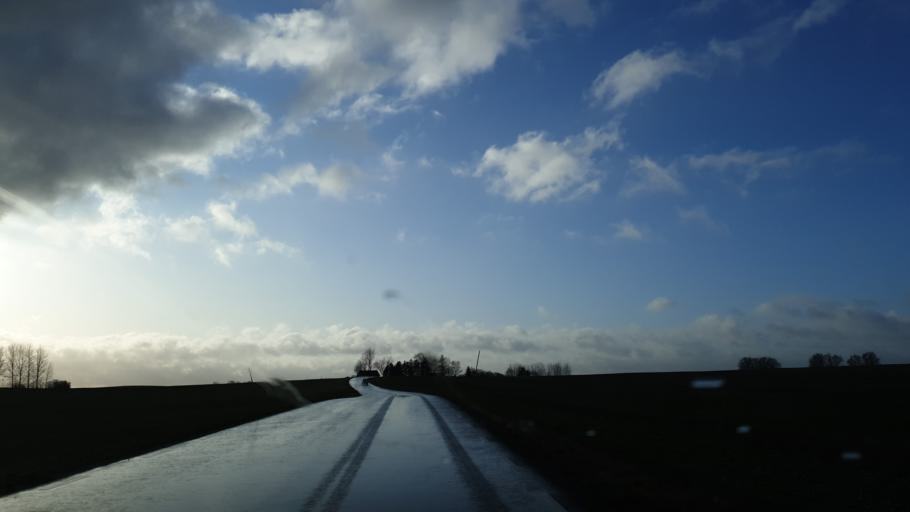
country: SE
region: Skane
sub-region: Skurups Kommun
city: Rydsgard
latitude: 55.4625
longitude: 13.5612
